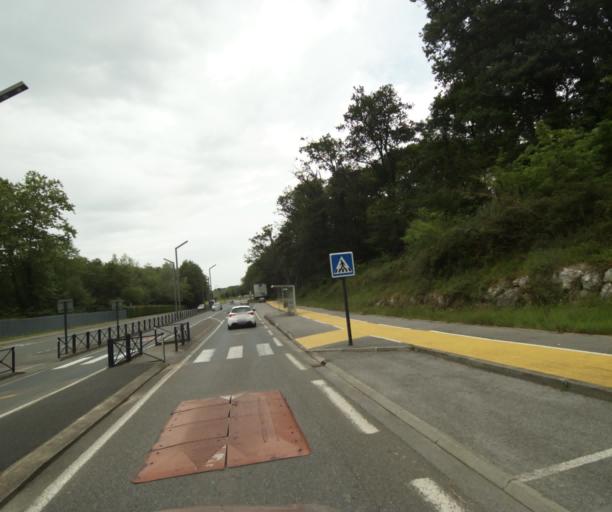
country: FR
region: Aquitaine
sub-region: Departement des Pyrenees-Atlantiques
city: Mouguerre
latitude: 43.4726
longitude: -1.4425
